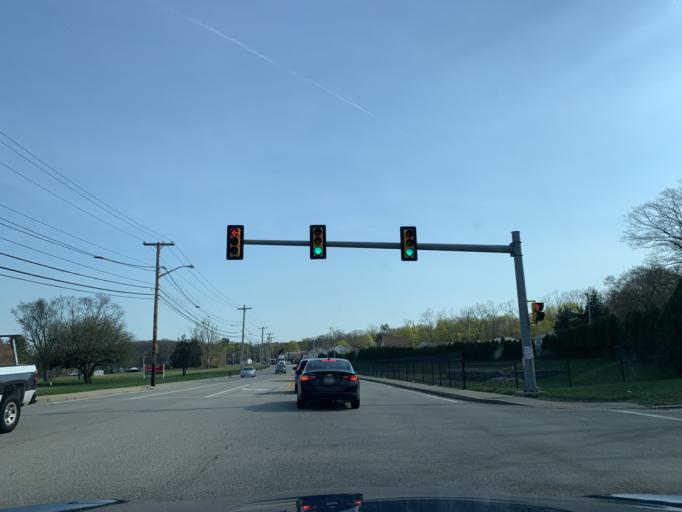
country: US
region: Rhode Island
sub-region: Providence County
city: Johnston
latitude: 41.8125
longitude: -71.4950
